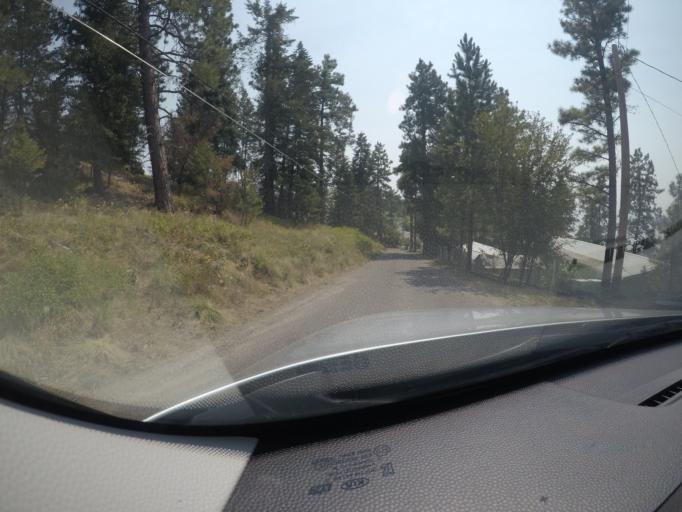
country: US
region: Montana
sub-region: Lake County
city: Polson
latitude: 47.7692
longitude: -114.1432
